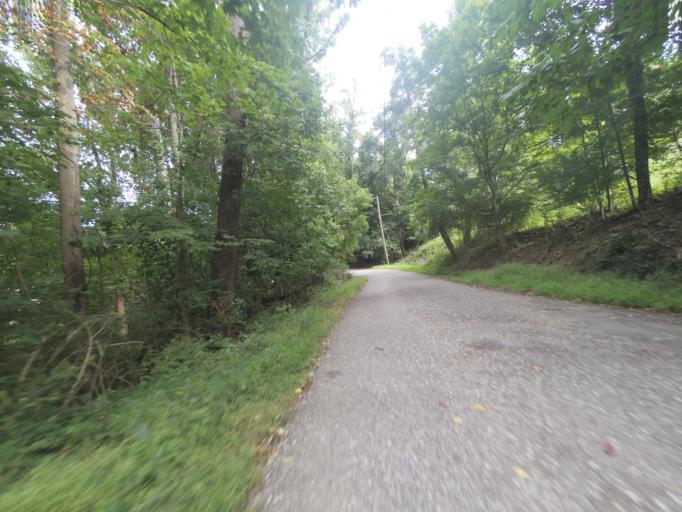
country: US
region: West Virginia
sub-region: Cabell County
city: Huntington
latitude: 38.4040
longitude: -82.4456
